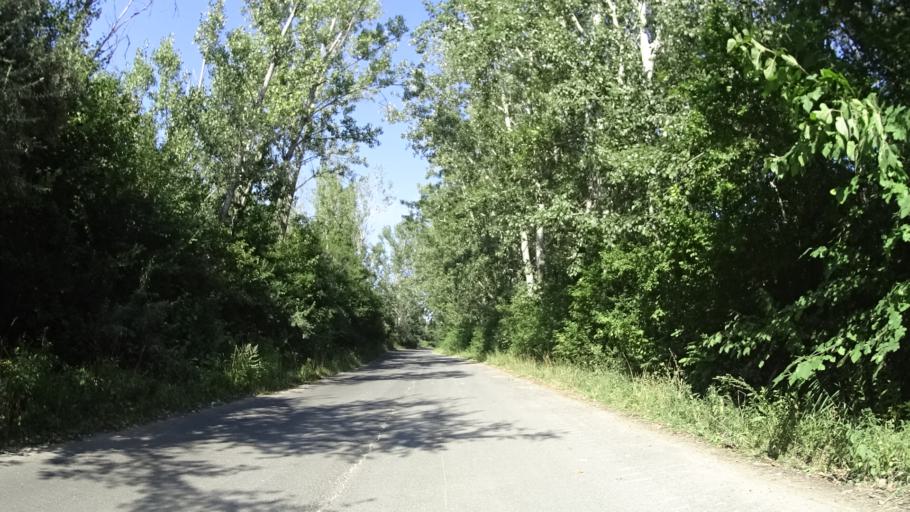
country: HU
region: Fejer
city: Gardony
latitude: 47.2373
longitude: 18.6242
